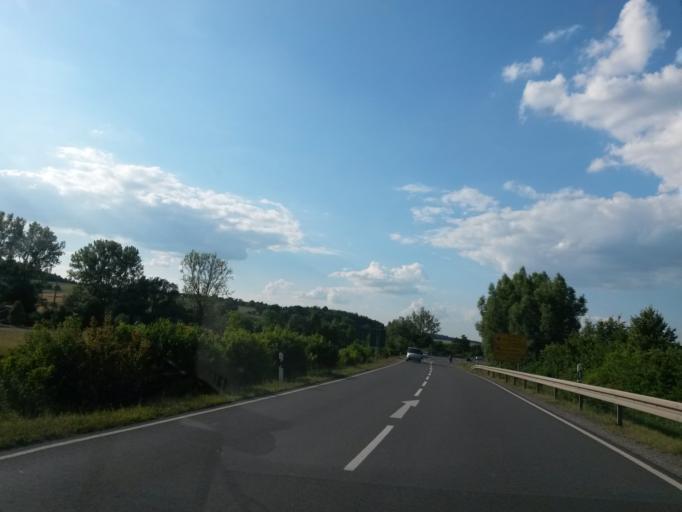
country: DE
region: Bavaria
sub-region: Regierungsbezirk Mittelfranken
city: Diespeck
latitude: 49.5919
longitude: 10.6234
